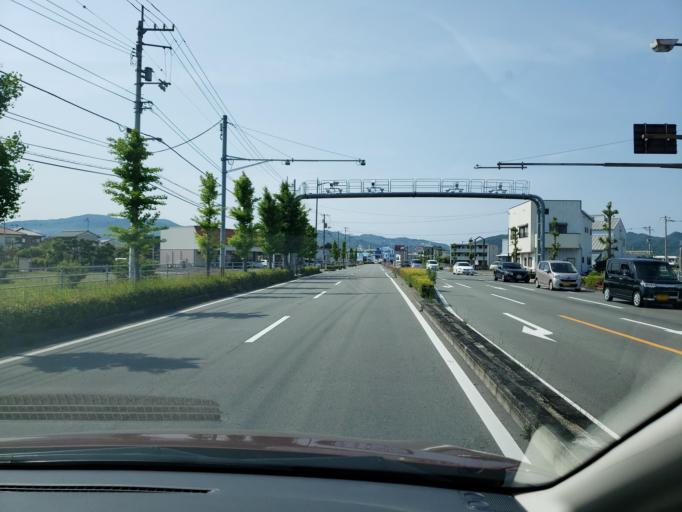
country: JP
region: Tokushima
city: Ishii
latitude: 34.1206
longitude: 134.4793
